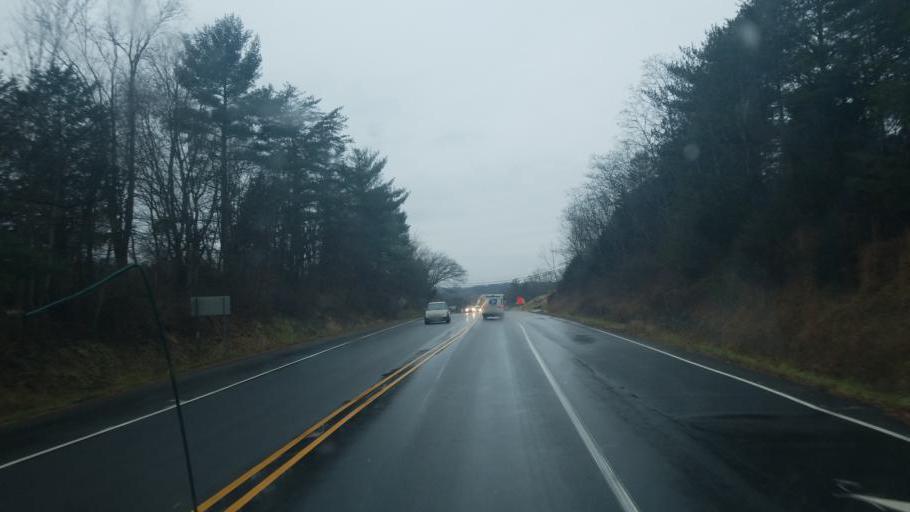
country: US
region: Indiana
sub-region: Brown County
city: Nashville
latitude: 39.2017
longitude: -86.2341
